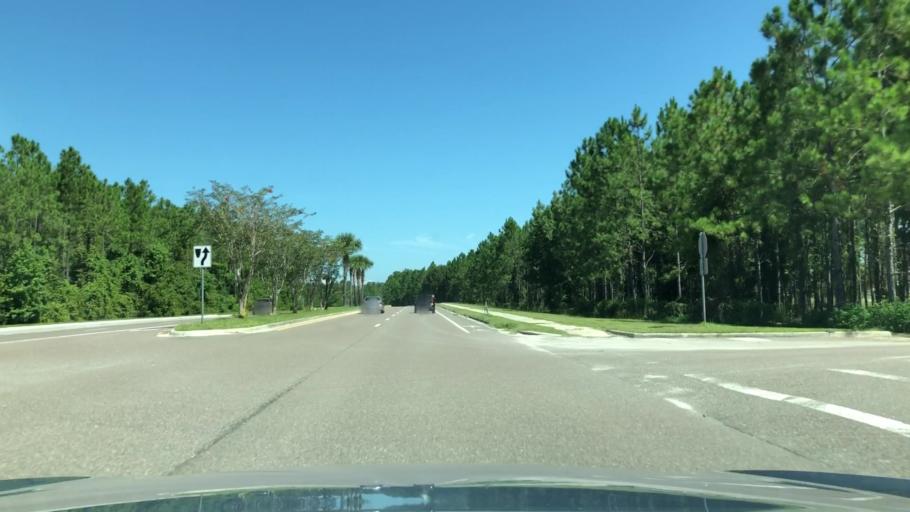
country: US
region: Florida
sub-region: Saint Johns County
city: Fruit Cove
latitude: 30.0965
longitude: -81.5380
